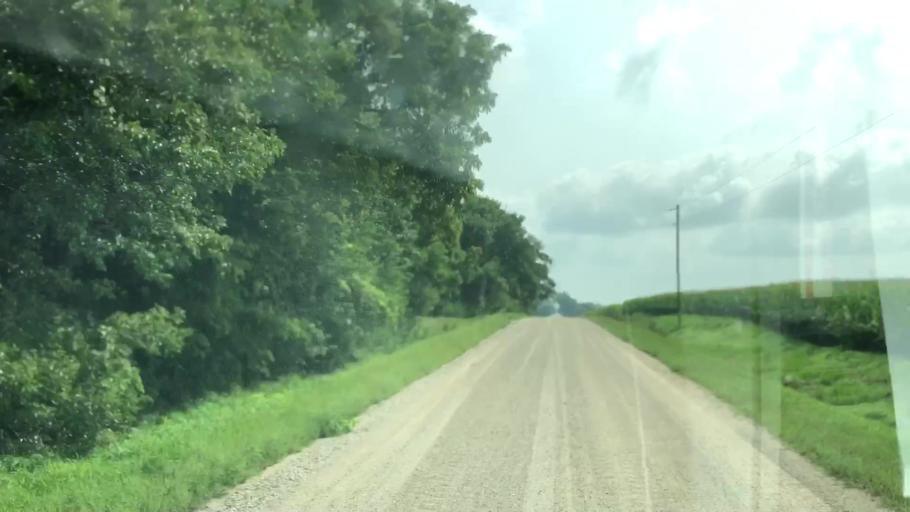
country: US
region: Iowa
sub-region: O'Brien County
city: Sheldon
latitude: 43.2004
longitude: -95.8990
